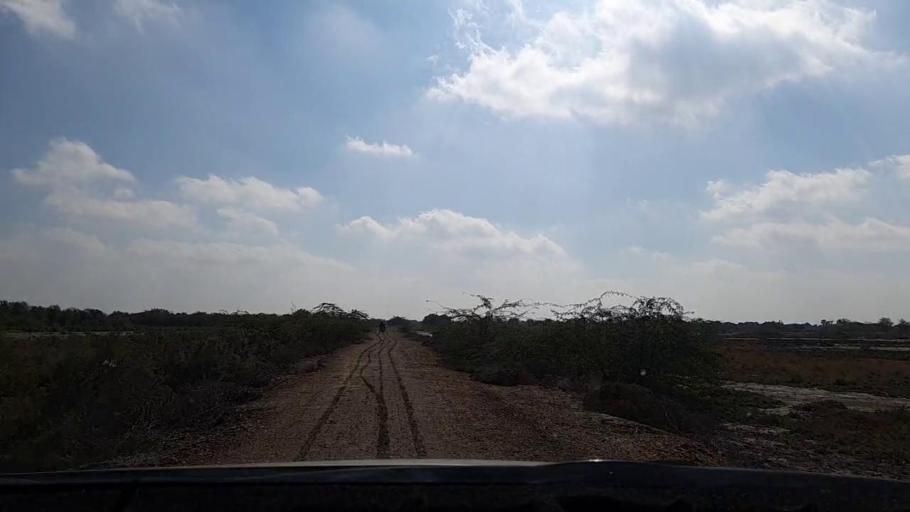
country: PK
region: Sindh
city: Pithoro
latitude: 25.7196
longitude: 69.2959
